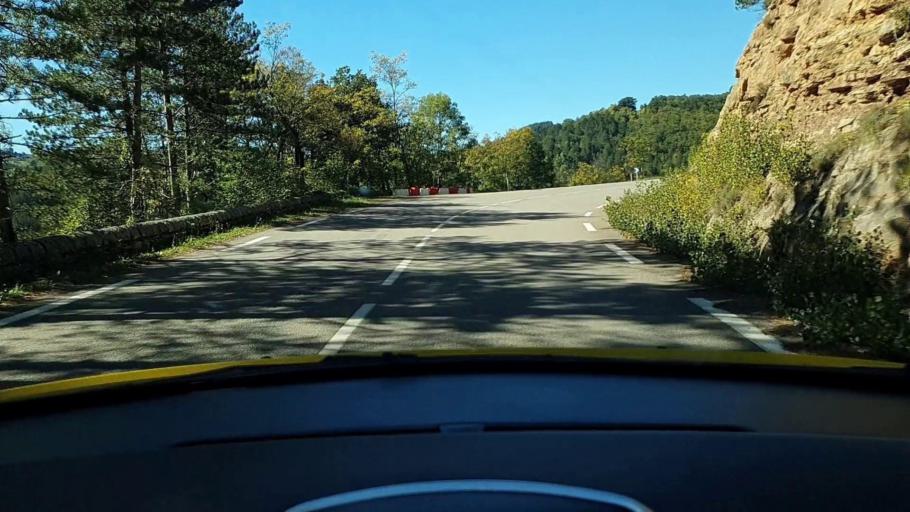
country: FR
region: Languedoc-Roussillon
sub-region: Departement du Gard
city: Le Vigan
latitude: 43.9674
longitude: 3.4424
